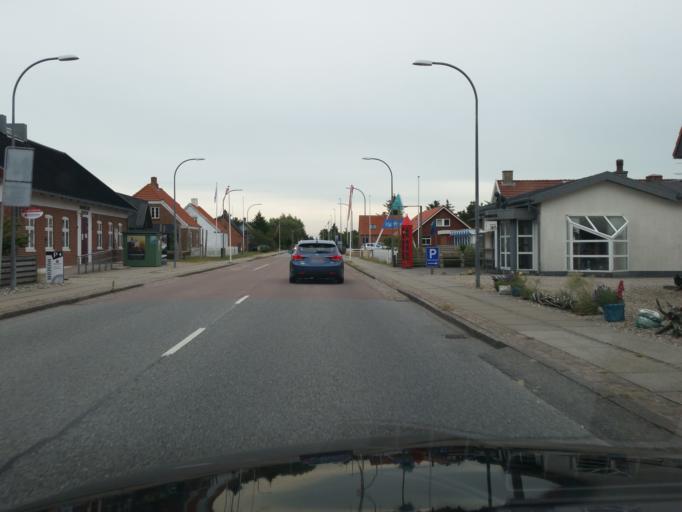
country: DK
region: Central Jutland
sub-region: Ringkobing-Skjern Kommune
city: Hvide Sande
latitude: 55.8169
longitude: 8.1966
